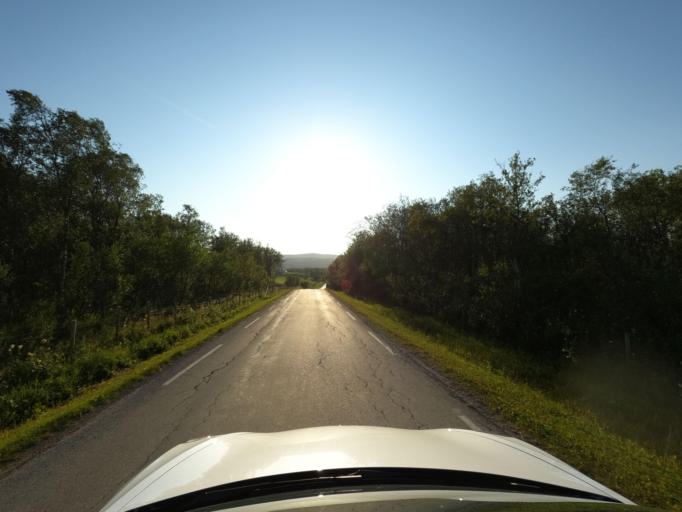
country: NO
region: Troms
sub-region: Skanland
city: Evenskjer
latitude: 68.4635
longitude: 16.6692
